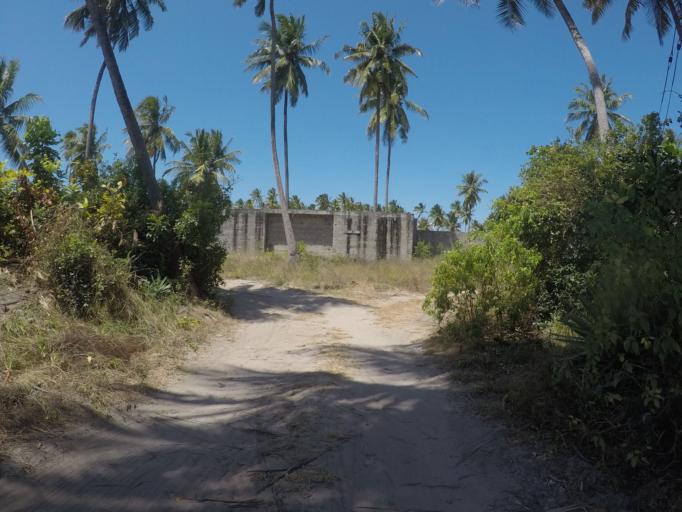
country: TZ
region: Zanzibar Central/South
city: Nganane
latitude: -6.2757
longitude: 39.5348
